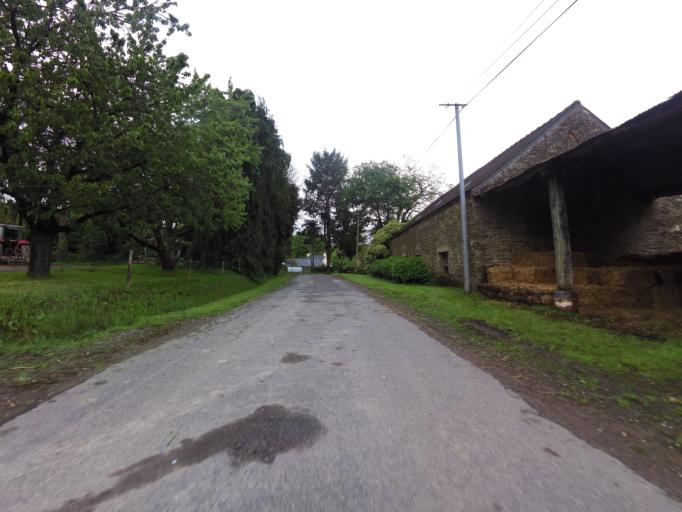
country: FR
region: Brittany
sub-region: Departement du Morbihan
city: Pluherlin
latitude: 47.7126
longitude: -2.3824
